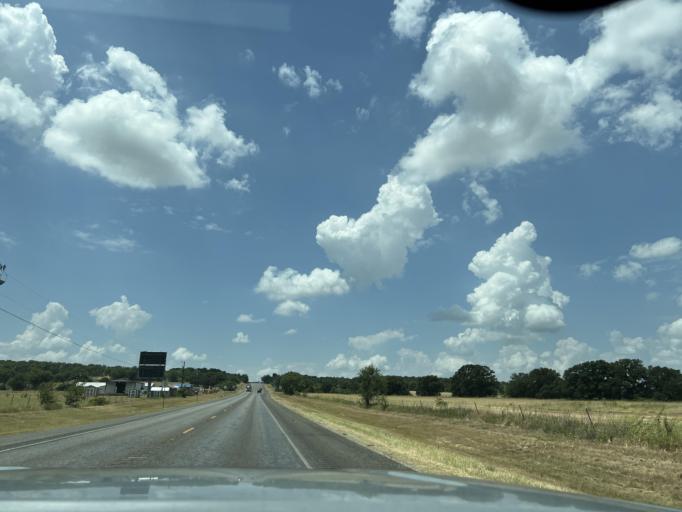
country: US
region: Texas
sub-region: Parker County
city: Springtown
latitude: 32.9394
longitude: -97.6967
